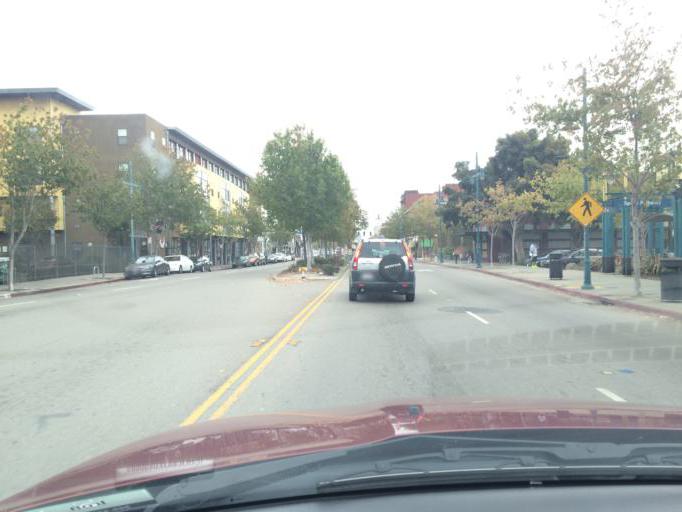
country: US
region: California
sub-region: Alameda County
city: Emeryville
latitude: 37.8303
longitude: -122.2797
